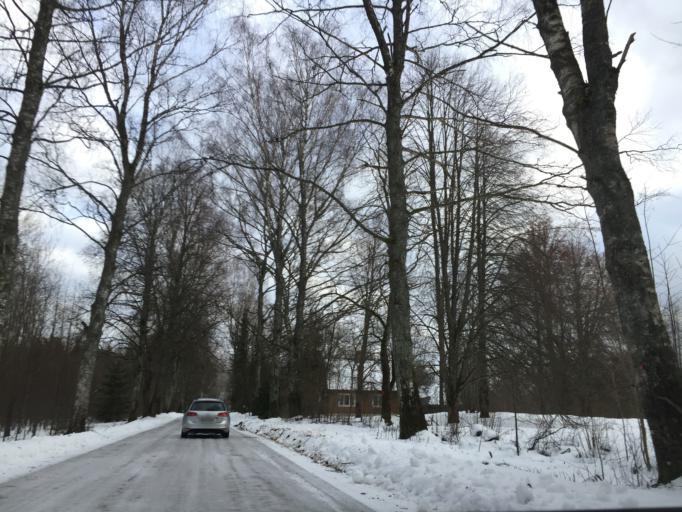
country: LV
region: Lielvarde
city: Lielvarde
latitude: 56.5799
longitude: 24.7785
